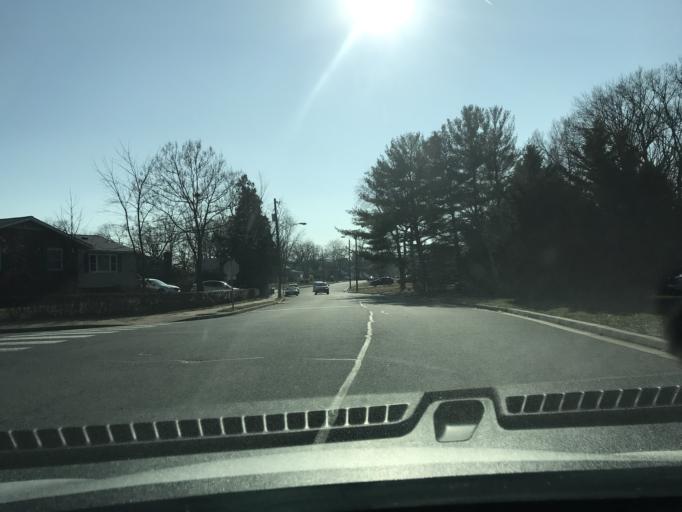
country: US
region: Virginia
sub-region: City of Fairfax
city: Fairfax
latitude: 38.8595
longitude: -77.3265
